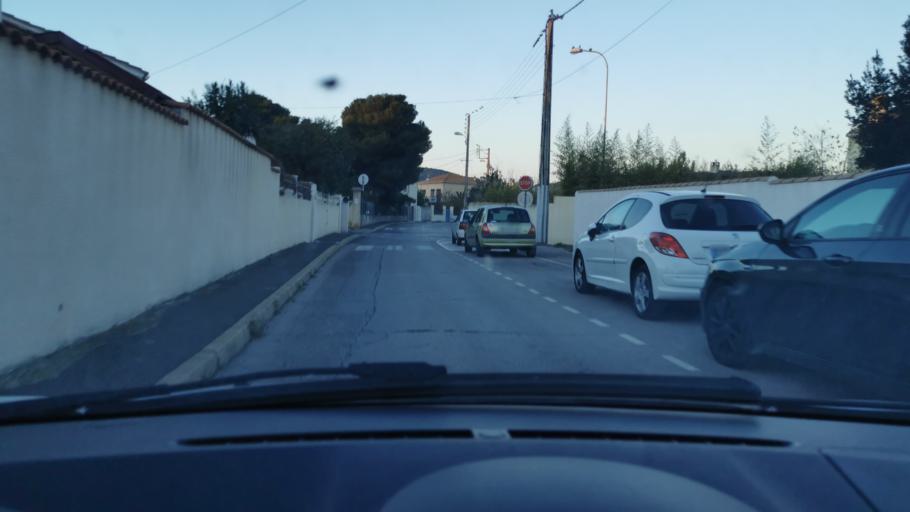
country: FR
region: Languedoc-Roussillon
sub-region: Departement de l'Herault
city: Frontignan
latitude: 43.4533
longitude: 3.7563
